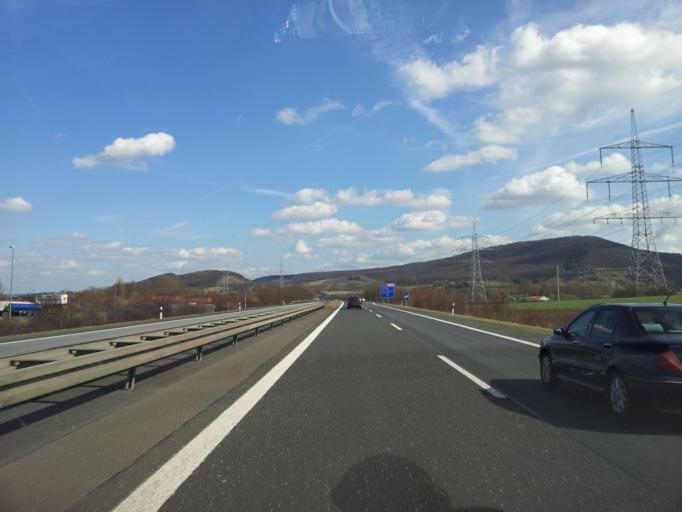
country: DE
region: Bavaria
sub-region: Regierungsbezirk Unterfranken
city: Knetzgau
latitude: 49.9806
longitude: 10.5500
